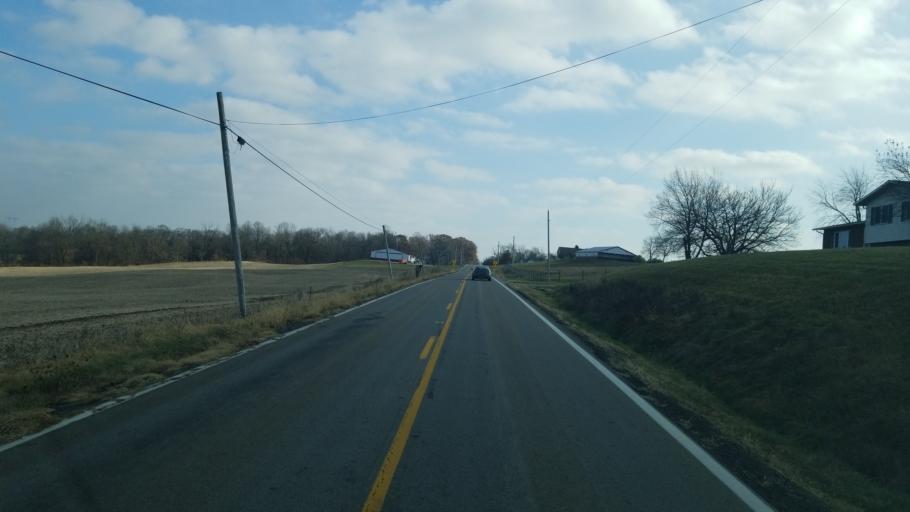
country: US
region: Ohio
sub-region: Licking County
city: Utica
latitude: 40.1732
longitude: -82.4957
